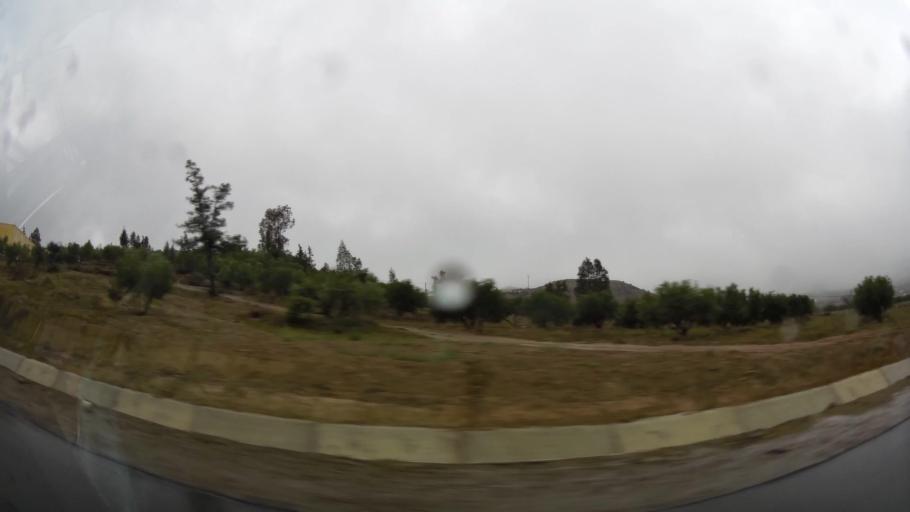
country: MA
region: Oriental
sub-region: Nador
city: Midar
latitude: 34.8300
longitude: -3.7196
